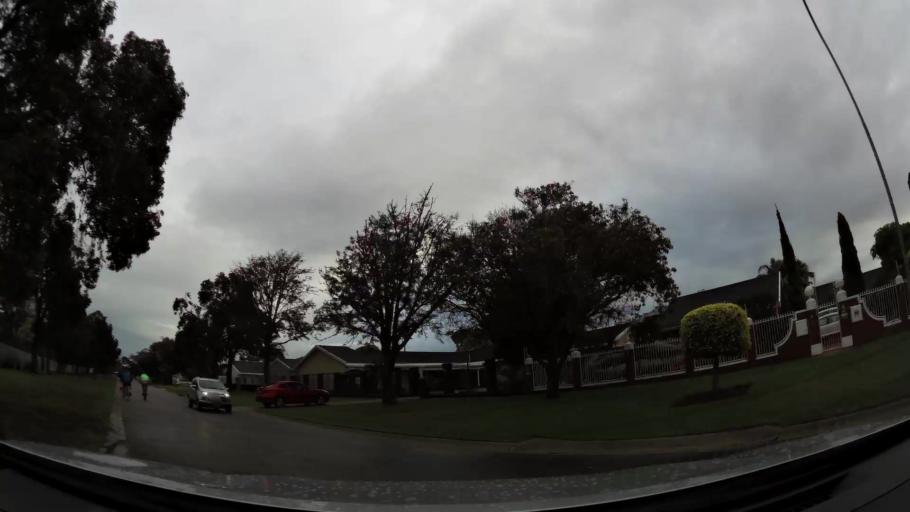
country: ZA
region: Eastern Cape
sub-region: Nelson Mandela Bay Metropolitan Municipality
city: Port Elizabeth
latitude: -33.9777
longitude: 25.5677
